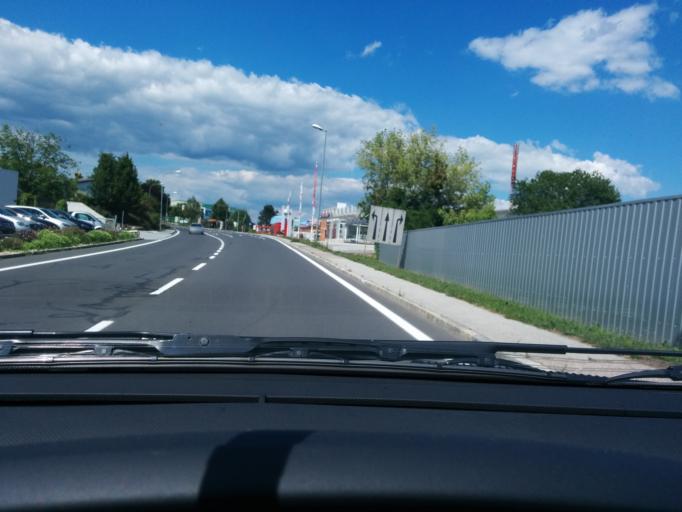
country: AT
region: Styria
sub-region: Politischer Bezirk Hartberg-Fuerstenfeld
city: Hartberg
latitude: 47.2860
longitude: 15.9788
